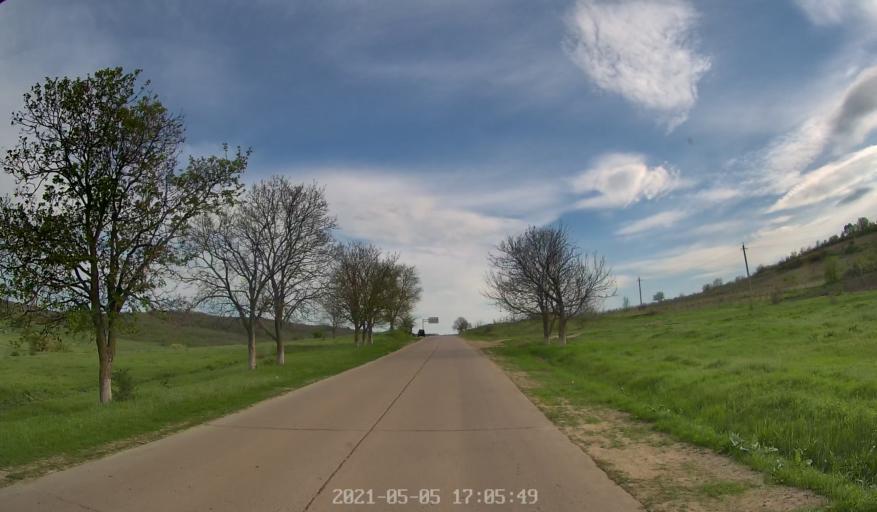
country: MD
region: Chisinau
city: Vadul lui Voda
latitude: 47.0261
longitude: 29.1396
